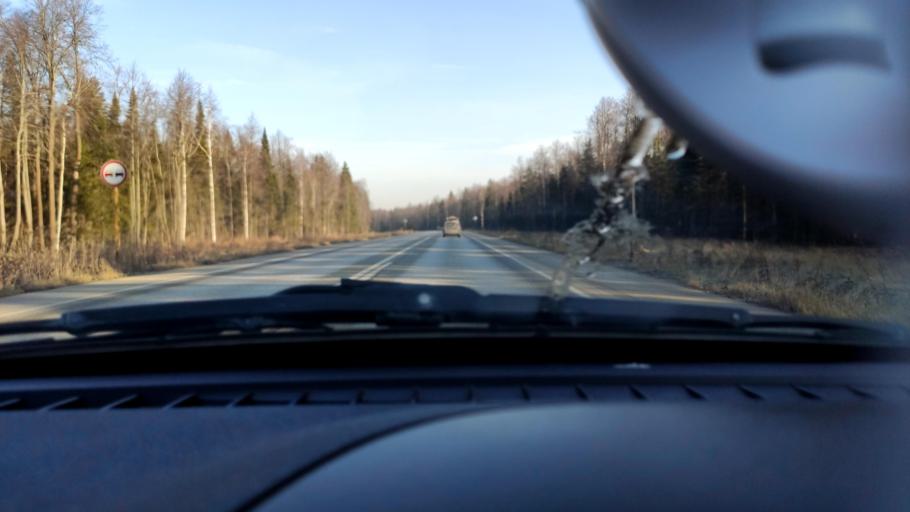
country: RU
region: Perm
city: Novyye Lyady
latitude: 58.0302
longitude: 56.5218
